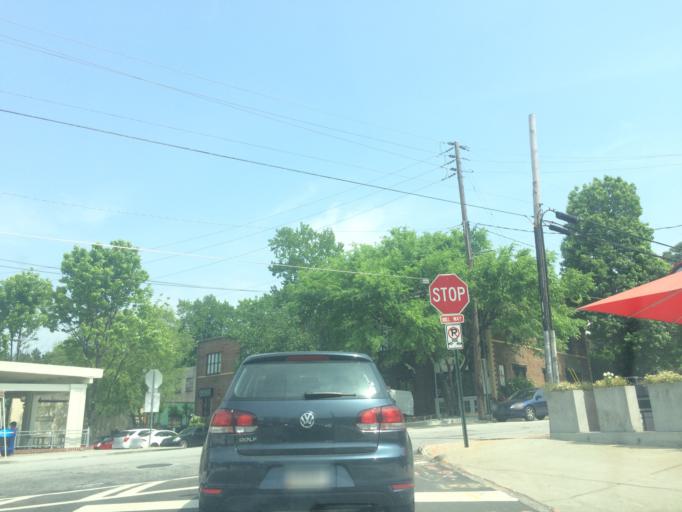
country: US
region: Georgia
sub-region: DeKalb County
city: Druid Hills
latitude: 33.7628
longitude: -84.3580
